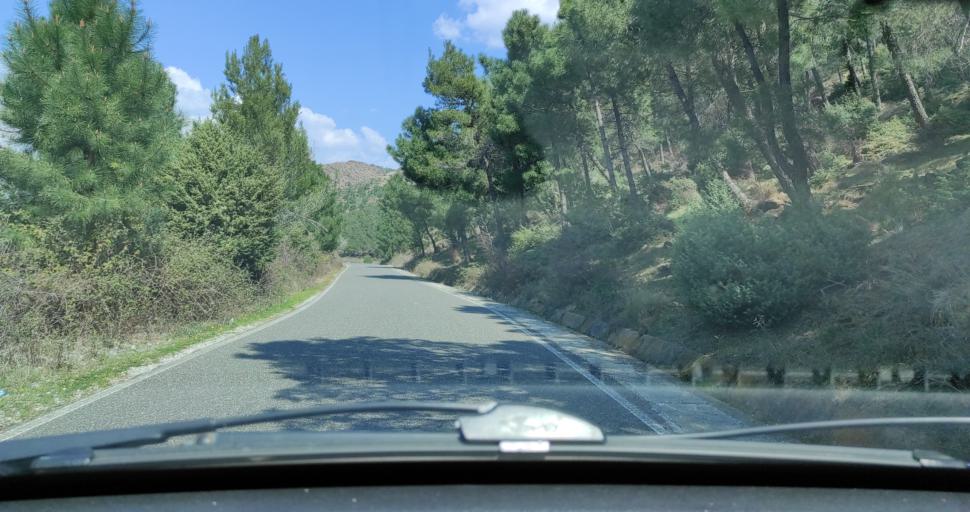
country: AL
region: Shkoder
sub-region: Rrethi i Shkodres
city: Vau i Dejes
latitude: 41.9933
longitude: 19.6473
